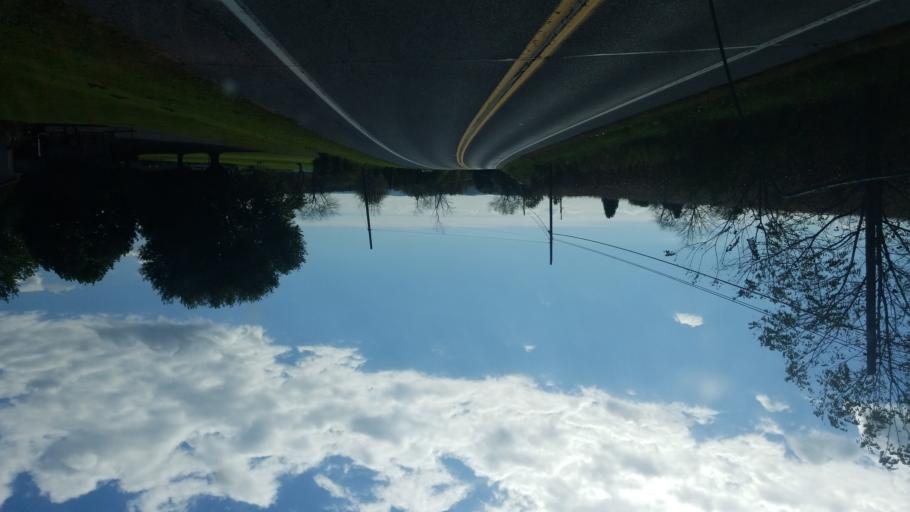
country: US
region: Pennsylvania
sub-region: Bedford County
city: Bedford
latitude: 40.1060
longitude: -78.5259
